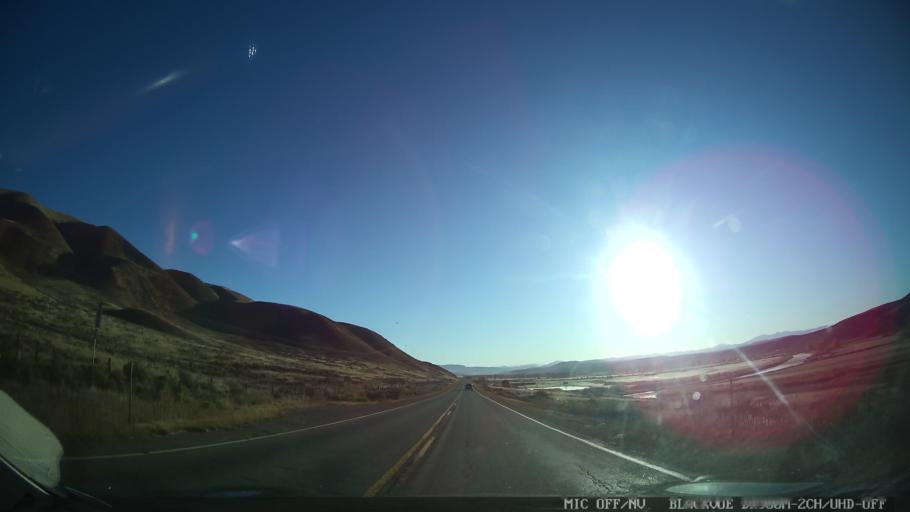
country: US
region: Colorado
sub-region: Grand County
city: Kremmling
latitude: 40.0505
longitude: -106.3480
